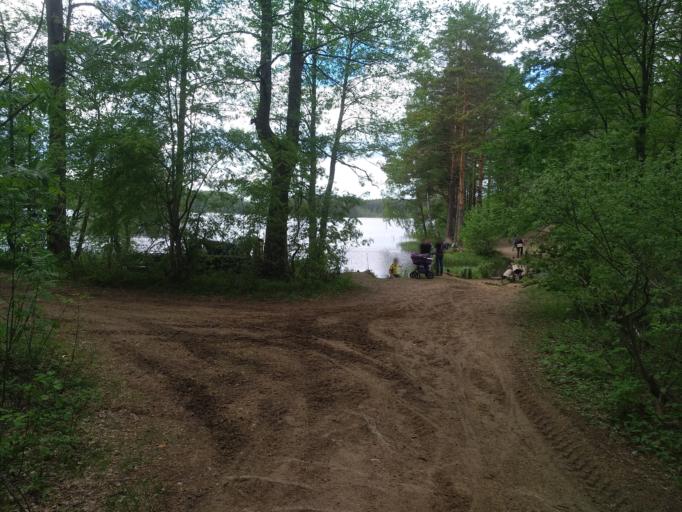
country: RU
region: Leningrad
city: Michurinskoye
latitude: 60.5975
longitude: 29.8773
